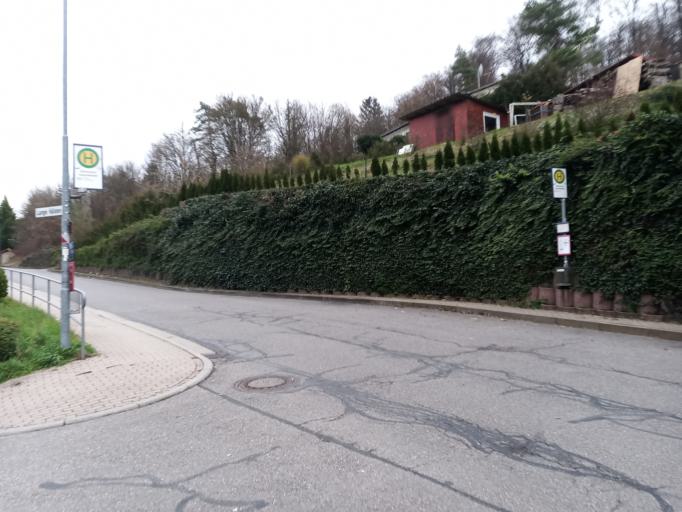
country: DE
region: Baden-Wuerttemberg
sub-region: Karlsruhe Region
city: Binau
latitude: 49.3607
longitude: 9.0512
